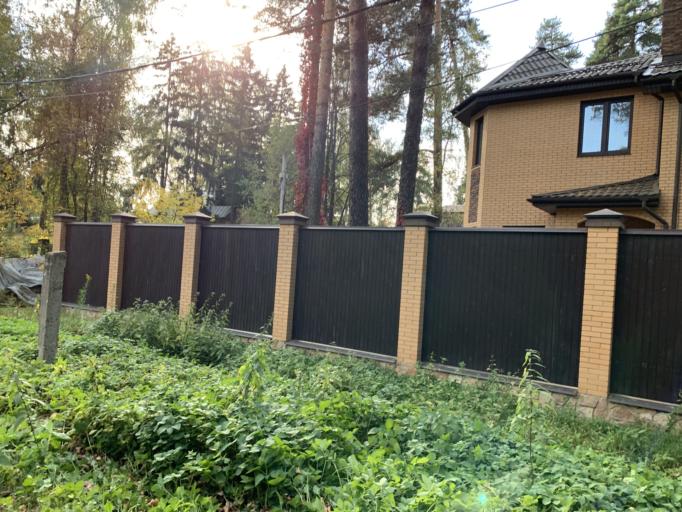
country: RU
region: Moskovskaya
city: Mamontovka
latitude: 55.9850
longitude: 37.8314
